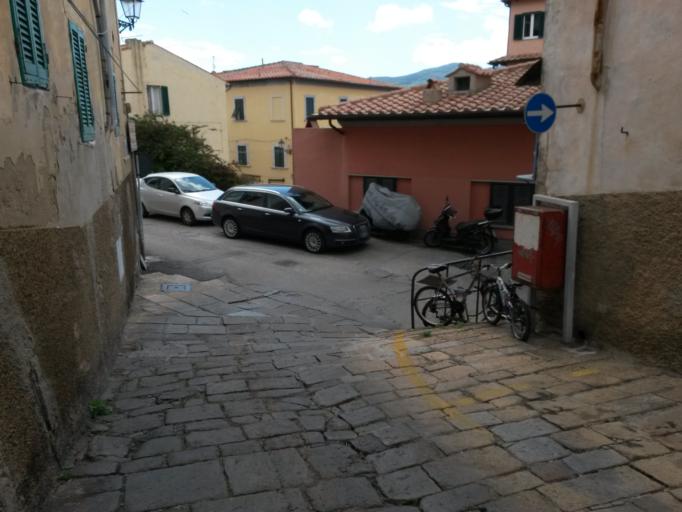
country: IT
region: Tuscany
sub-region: Provincia di Livorno
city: Portoferraio
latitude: 42.8153
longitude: 10.3326
